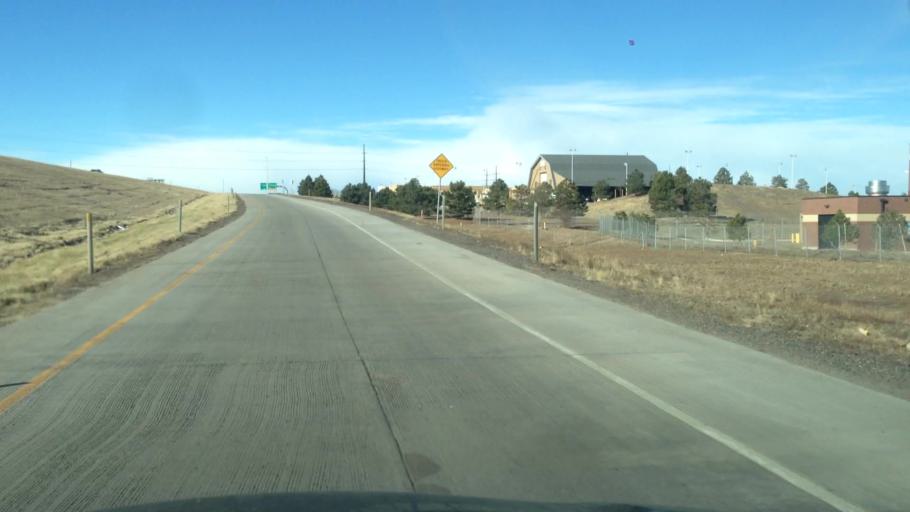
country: US
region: Colorado
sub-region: Douglas County
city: Stonegate
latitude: 39.5497
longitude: -104.7940
